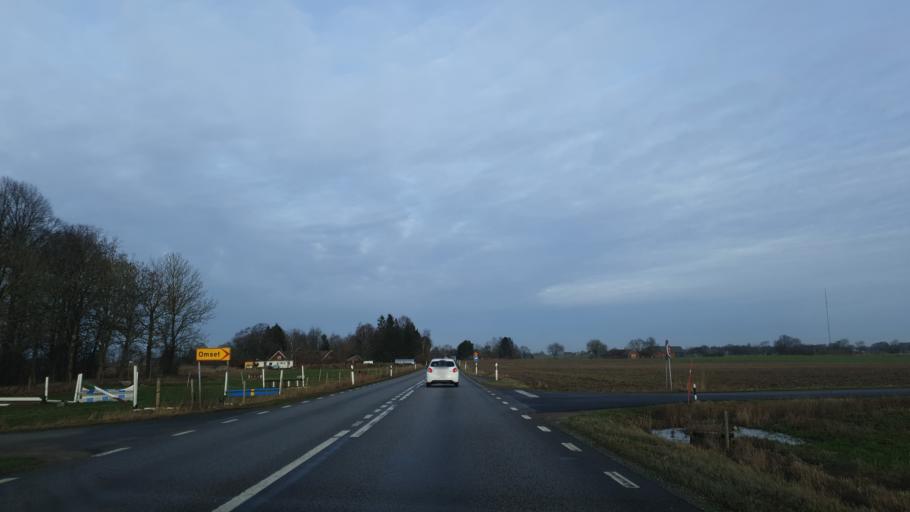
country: SE
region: Skane
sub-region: Horby Kommun
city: Hoerby
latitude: 55.7794
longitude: 13.6753
